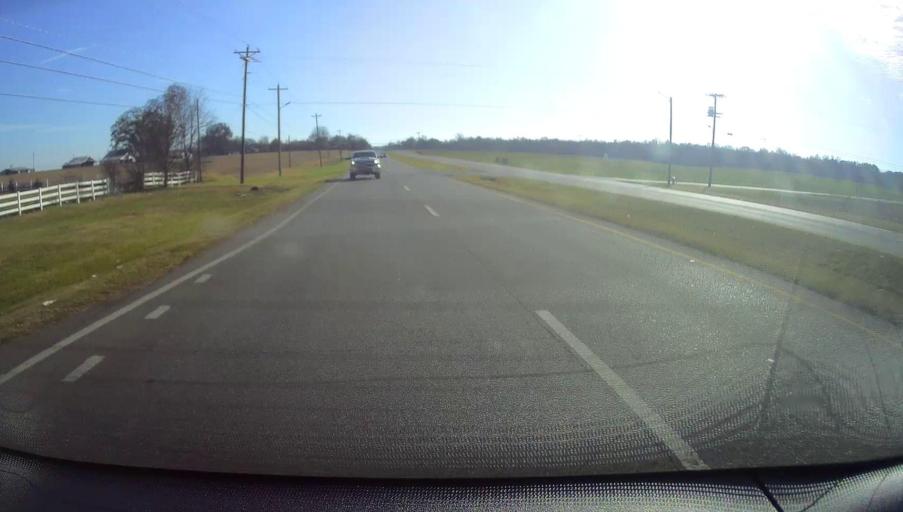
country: US
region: Alabama
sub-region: Limestone County
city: Athens
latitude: 34.7462
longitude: -86.9570
